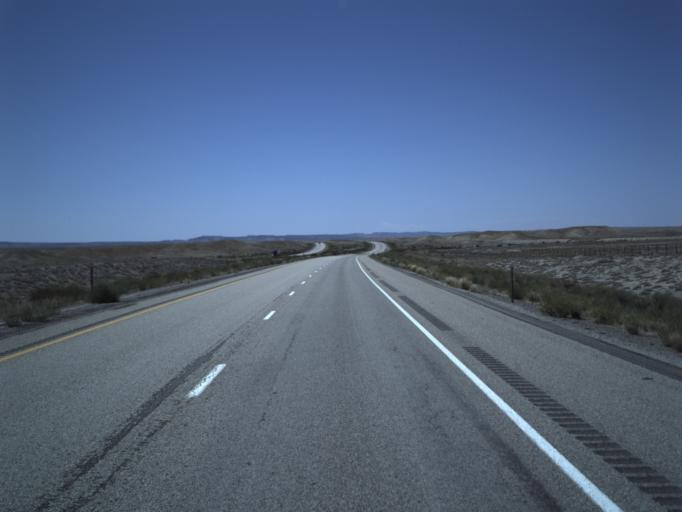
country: US
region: Utah
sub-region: Grand County
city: Moab
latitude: 39.0022
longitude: -109.3182
